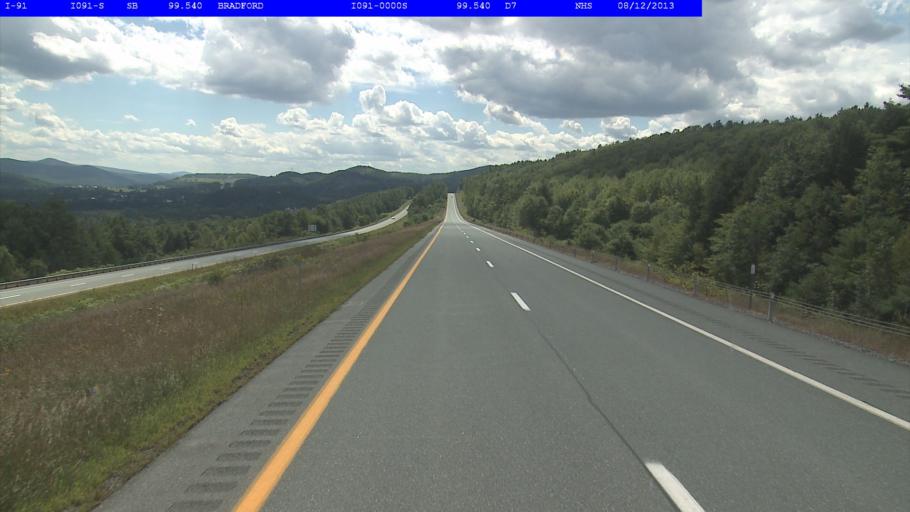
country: US
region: New Hampshire
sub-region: Grafton County
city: Haverhill
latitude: 44.0093
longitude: -72.1252
